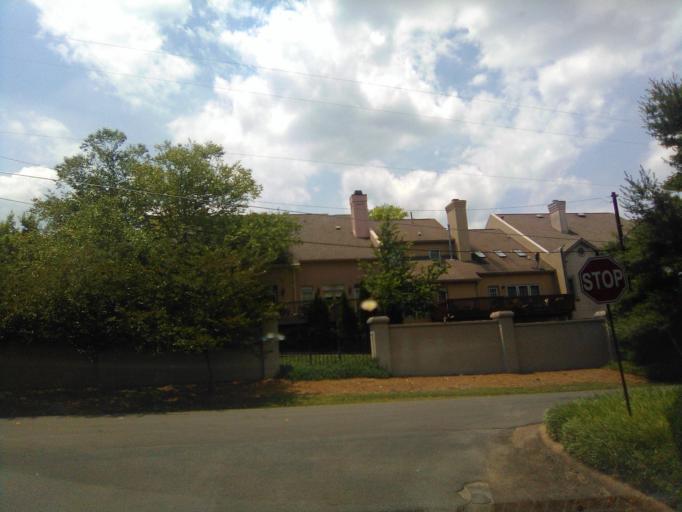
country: US
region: Tennessee
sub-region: Davidson County
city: Belle Meade
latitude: 36.1272
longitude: -86.8285
